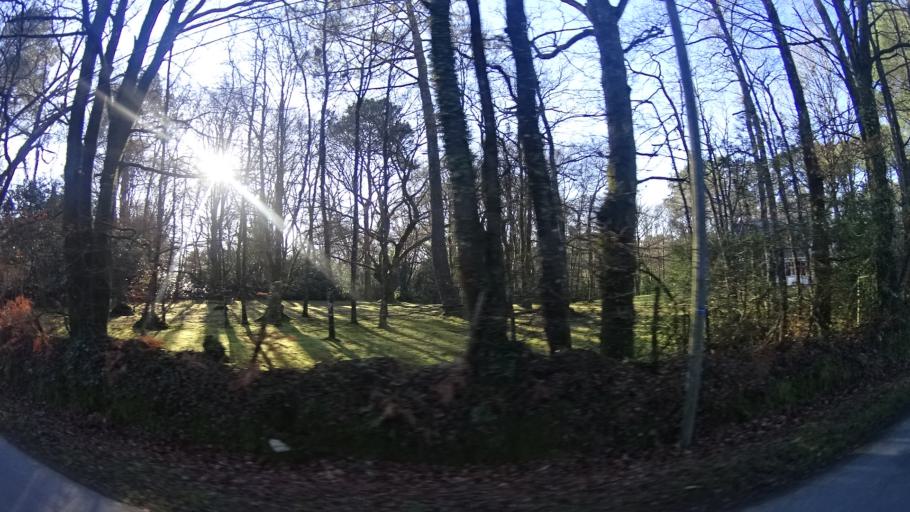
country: FR
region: Brittany
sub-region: Departement du Morbihan
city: Allaire
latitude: 47.6431
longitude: -2.1764
